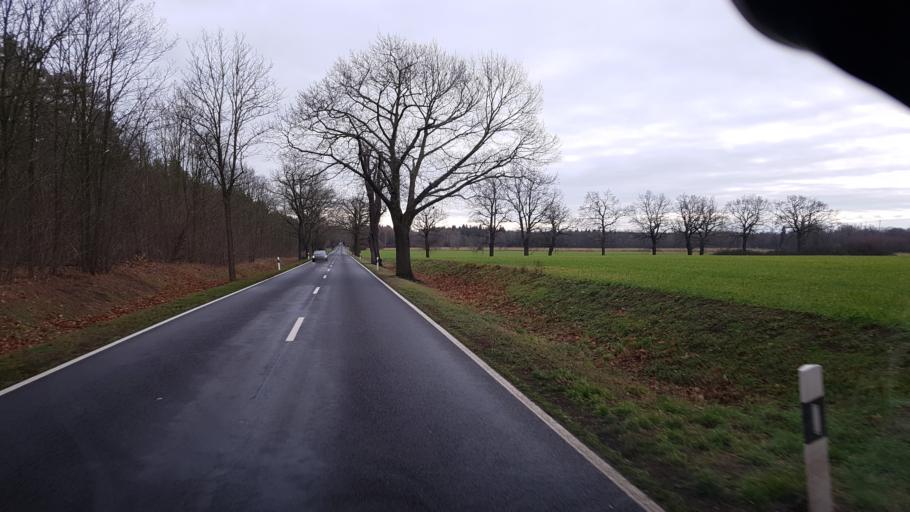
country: DE
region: Brandenburg
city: Altdobern
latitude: 51.6753
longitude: 14.0304
